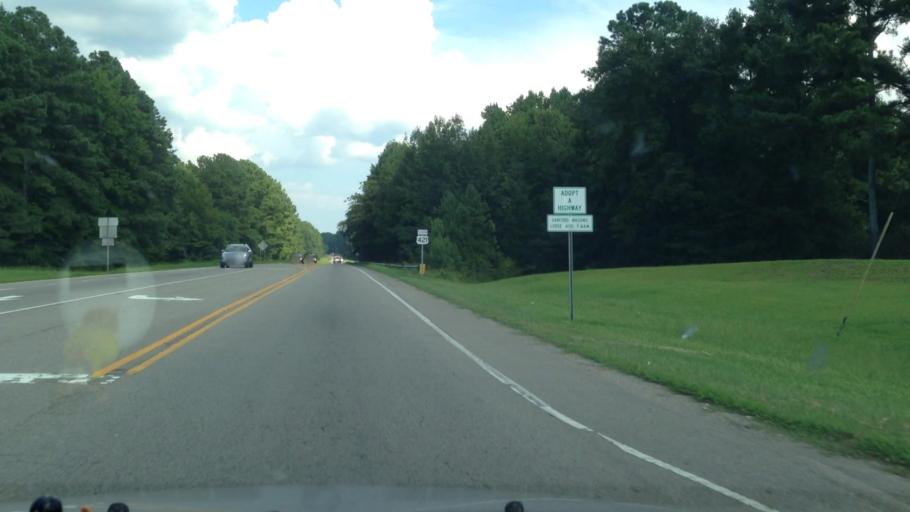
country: US
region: North Carolina
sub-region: Lee County
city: Broadway
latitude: 35.4443
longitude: -79.1098
